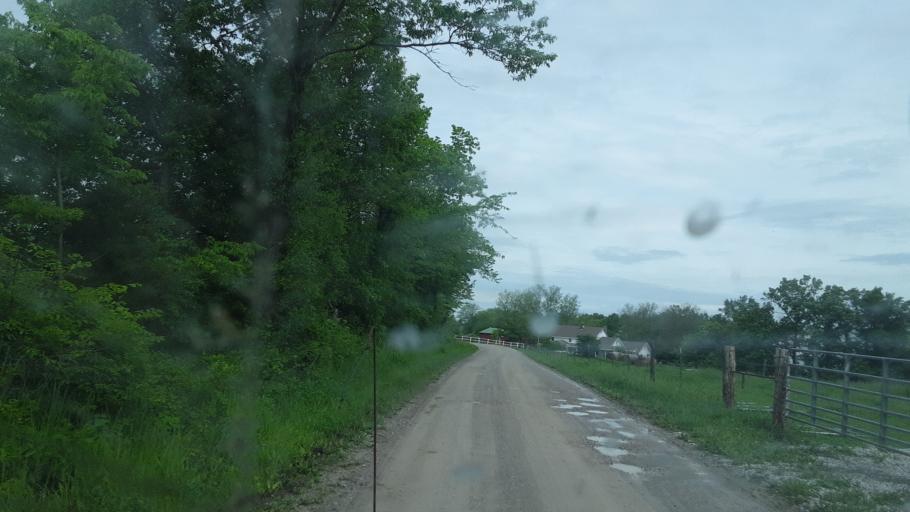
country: US
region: Missouri
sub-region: Clark County
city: Kahoka
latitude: 40.4267
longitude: -91.6098
